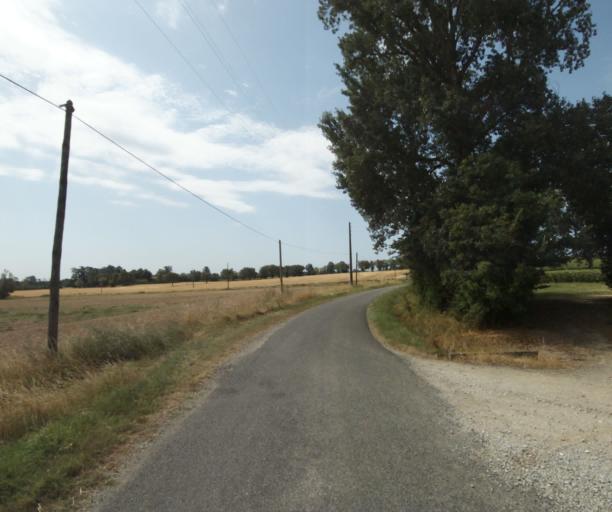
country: FR
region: Midi-Pyrenees
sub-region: Departement de la Haute-Garonne
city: Saint-Felix-Lauragais
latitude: 43.4369
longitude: 1.9051
